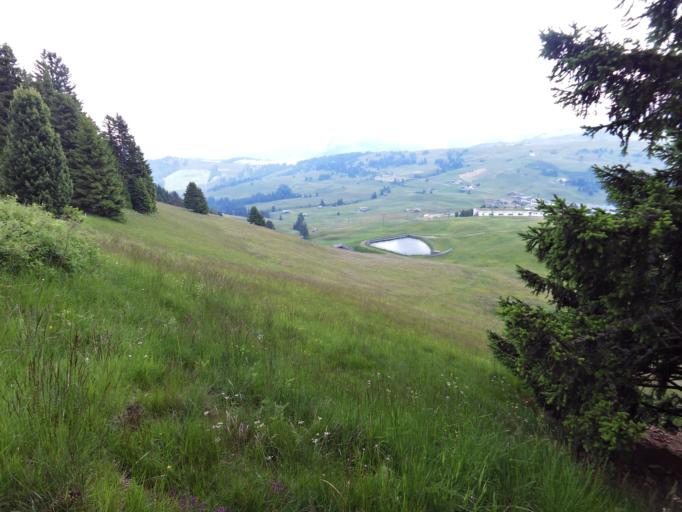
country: IT
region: Trentino-Alto Adige
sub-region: Bolzano
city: Siusi
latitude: 46.5467
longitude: 11.6127
